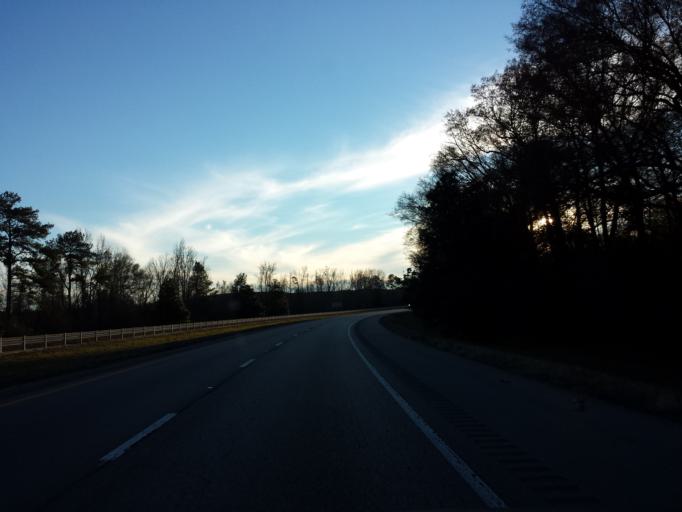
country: US
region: Alabama
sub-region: Sumter County
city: York
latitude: 32.4155
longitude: -88.4598
